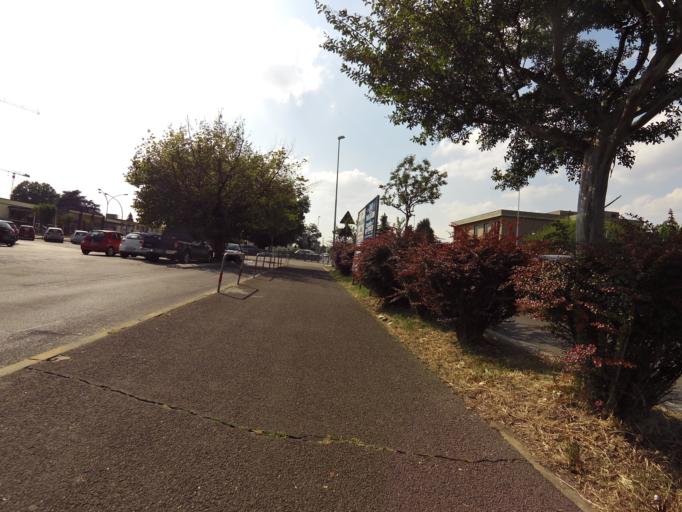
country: IT
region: Lombardy
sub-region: Provincia di Cremona
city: Crema
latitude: 45.3546
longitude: 9.6819
